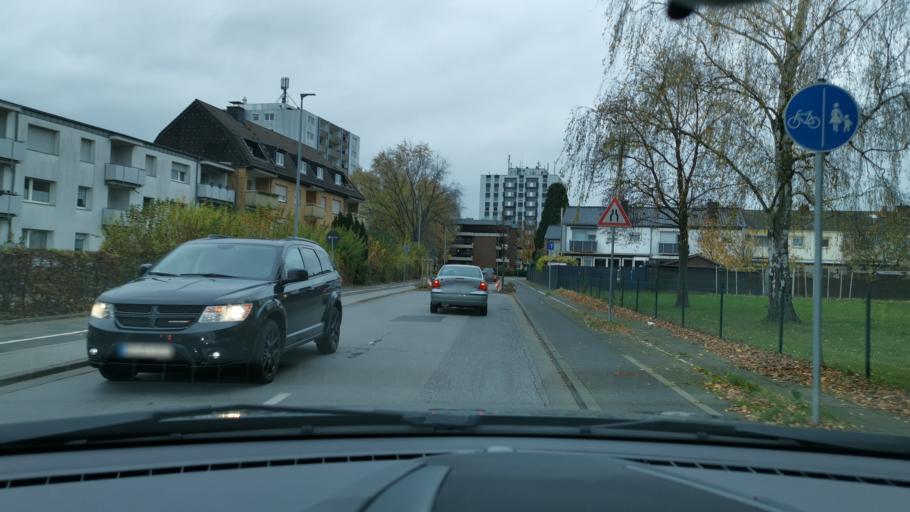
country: DE
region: North Rhine-Westphalia
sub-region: Regierungsbezirk Dusseldorf
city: Grevenbroich
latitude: 51.0780
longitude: 6.5972
